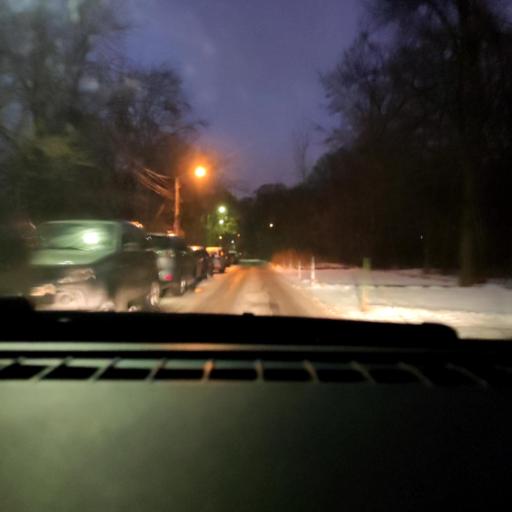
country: RU
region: Voronezj
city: Voronezh
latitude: 51.7032
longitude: 39.2230
